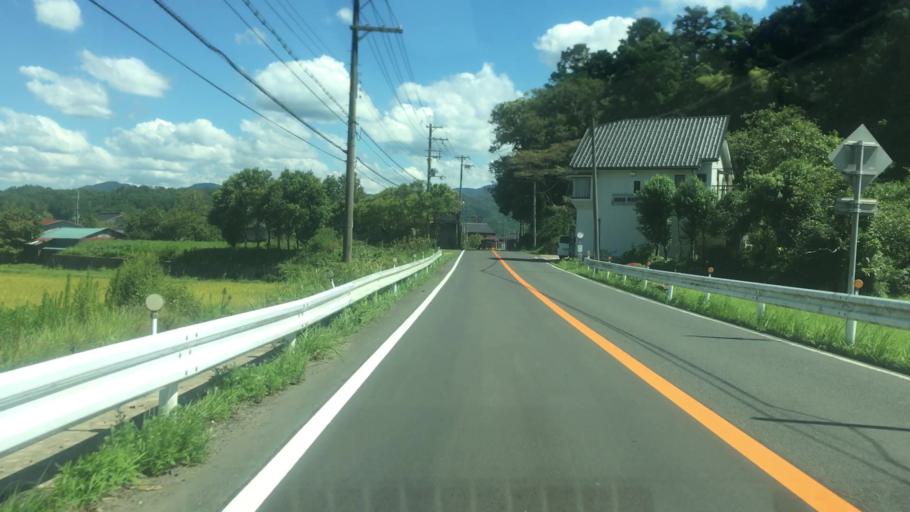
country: JP
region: Hyogo
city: Toyooka
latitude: 35.5932
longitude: 134.9210
